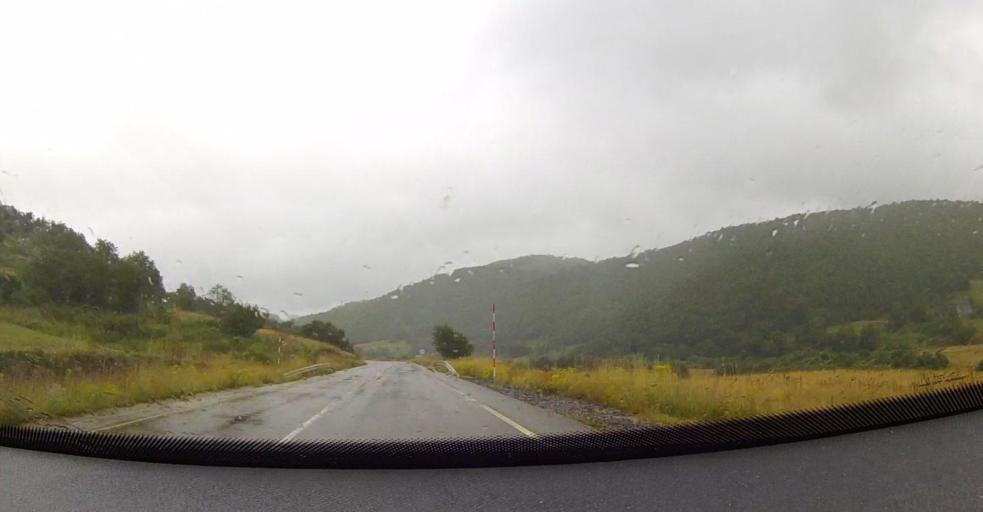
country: ES
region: Castille and Leon
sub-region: Provincia de Leon
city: Marana
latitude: 43.0695
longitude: -5.1822
